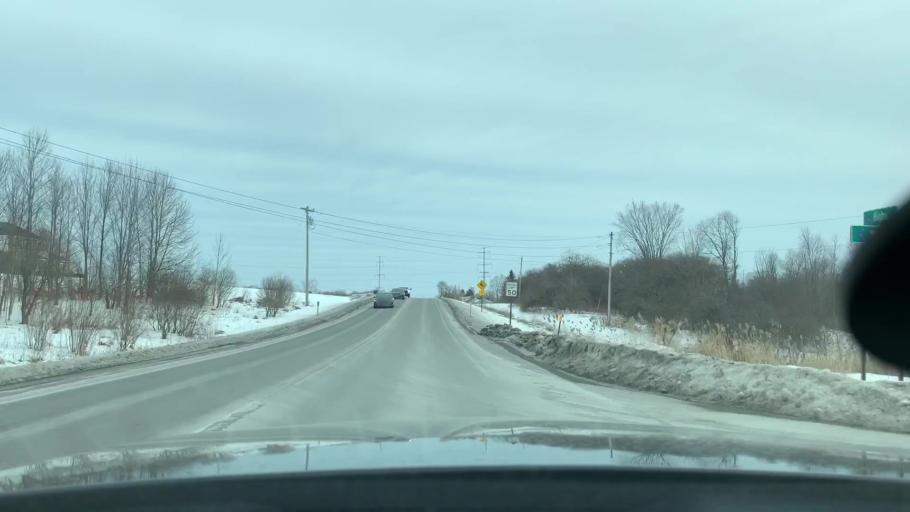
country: US
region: New York
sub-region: Herkimer County
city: Frankfort
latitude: 43.0327
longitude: -75.1372
